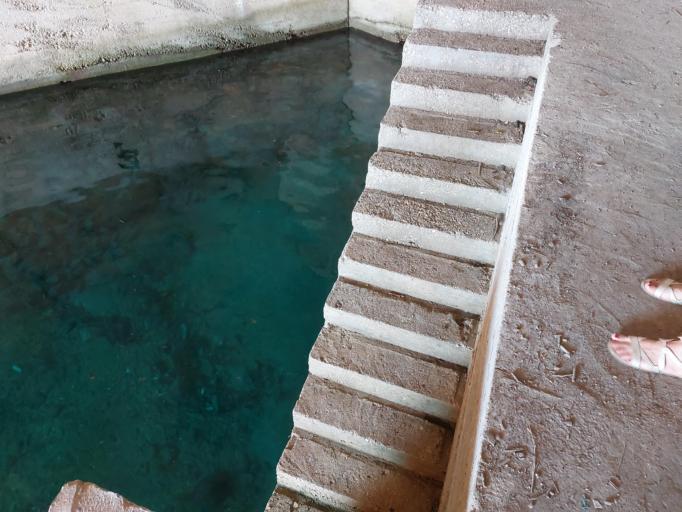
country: HR
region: Dubrovacko-Neretvanska
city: Smokvica
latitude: 42.7678
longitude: 16.8027
